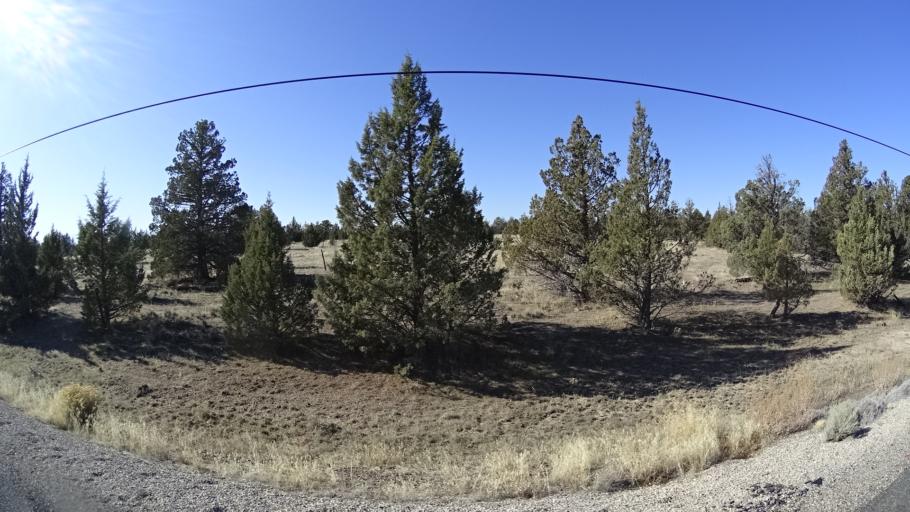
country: US
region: California
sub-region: Siskiyou County
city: Montague
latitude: 41.6572
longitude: -122.3649
